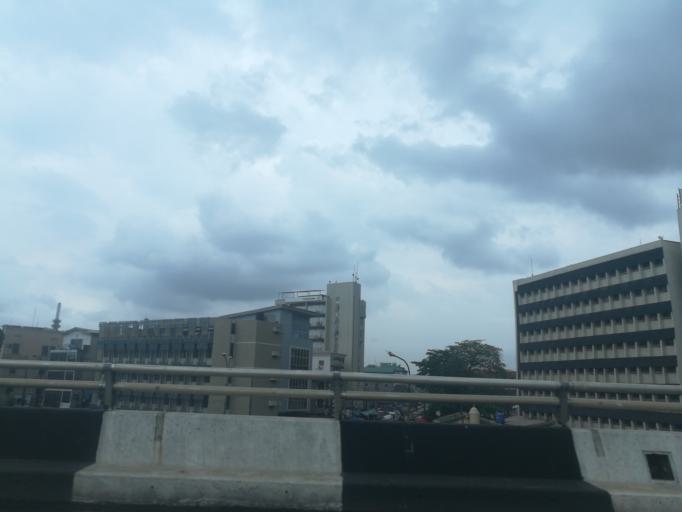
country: NG
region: Lagos
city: Lagos
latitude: 6.4494
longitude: 3.4078
